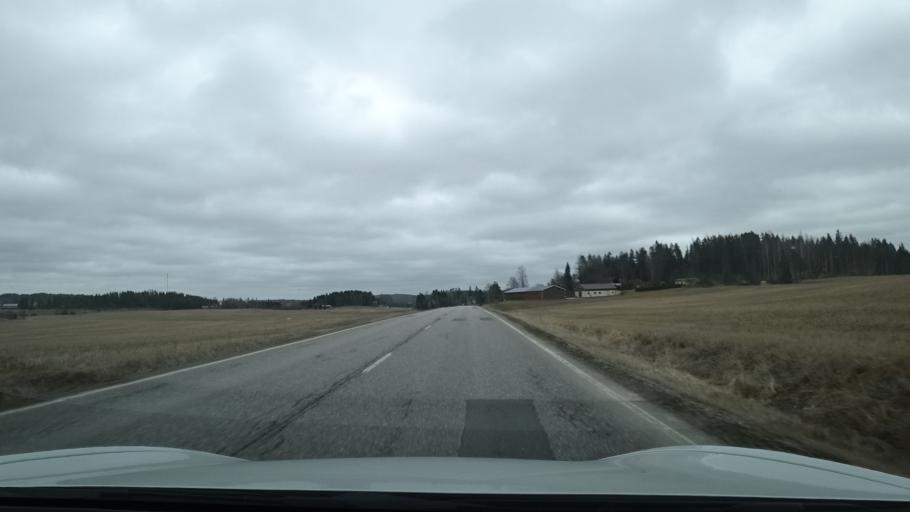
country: FI
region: Uusimaa
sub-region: Porvoo
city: Myrskylae
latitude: 60.6591
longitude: 25.8179
